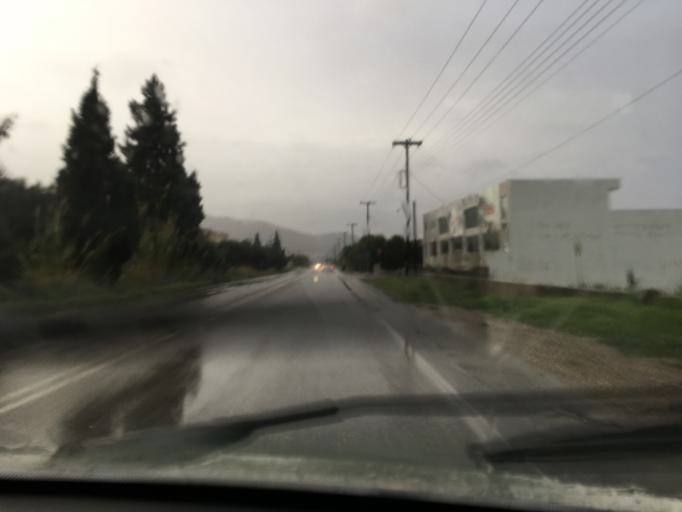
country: GR
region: West Greece
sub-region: Nomos Aitolias kai Akarnanias
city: Antirrio
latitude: 38.3563
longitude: 21.7751
